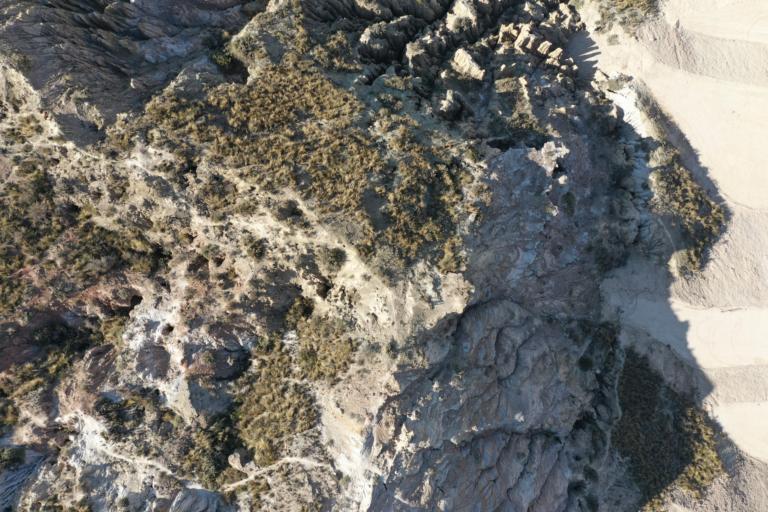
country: BO
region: La Paz
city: La Paz
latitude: -16.5597
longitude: -68.1236
